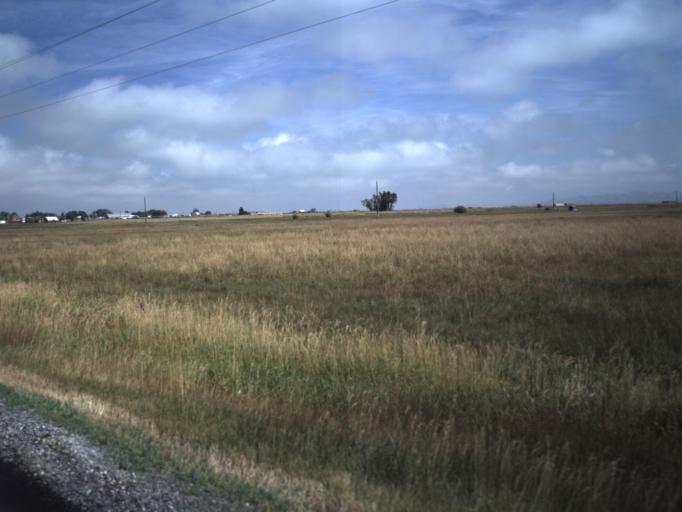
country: US
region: Utah
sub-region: Rich County
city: Randolph
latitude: 41.6488
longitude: -111.1841
